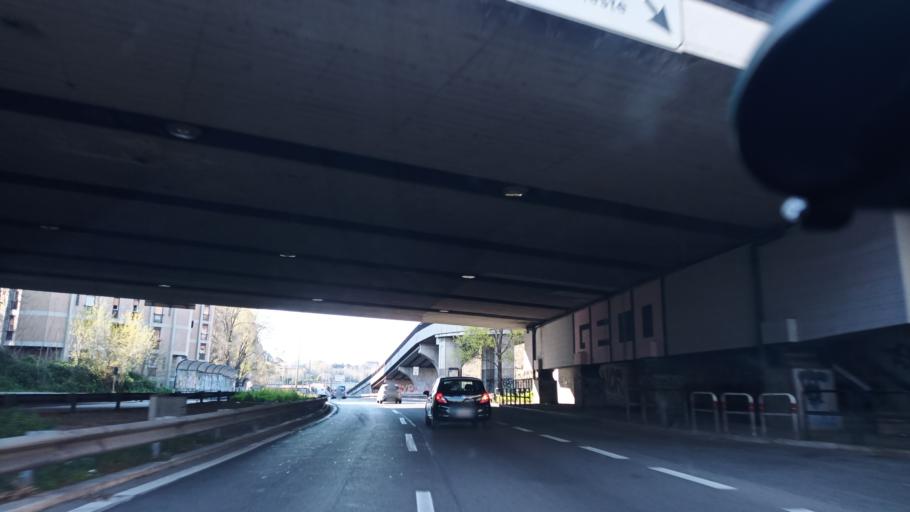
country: IT
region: Latium
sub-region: Citta metropolitana di Roma Capitale
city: Rome
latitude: 41.9299
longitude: 12.5270
